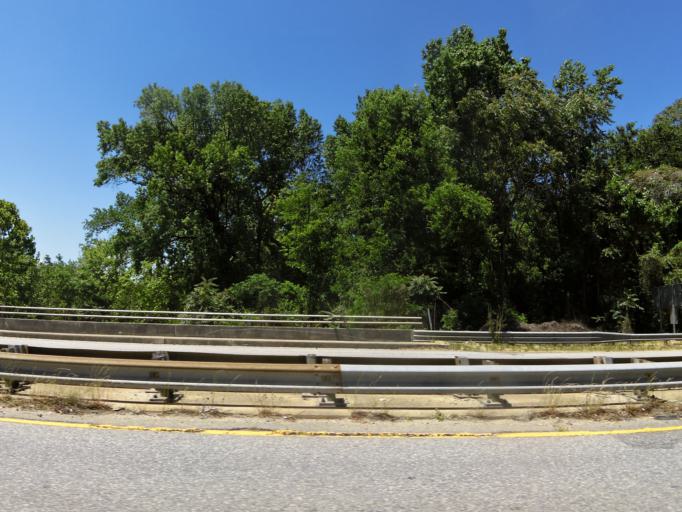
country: US
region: South Carolina
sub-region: Aiken County
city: North Augusta
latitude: 33.4819
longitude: -81.9503
